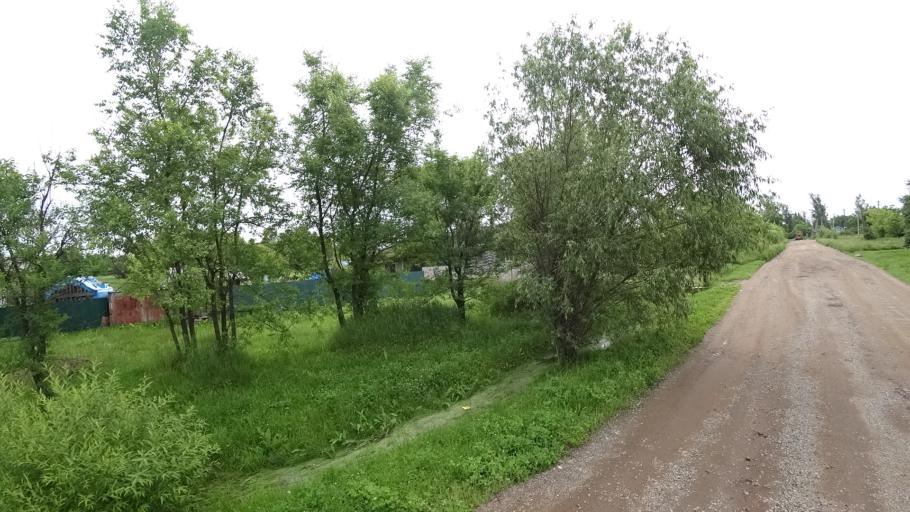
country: RU
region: Primorskiy
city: Novosysoyevka
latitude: 44.2495
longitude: 133.3769
